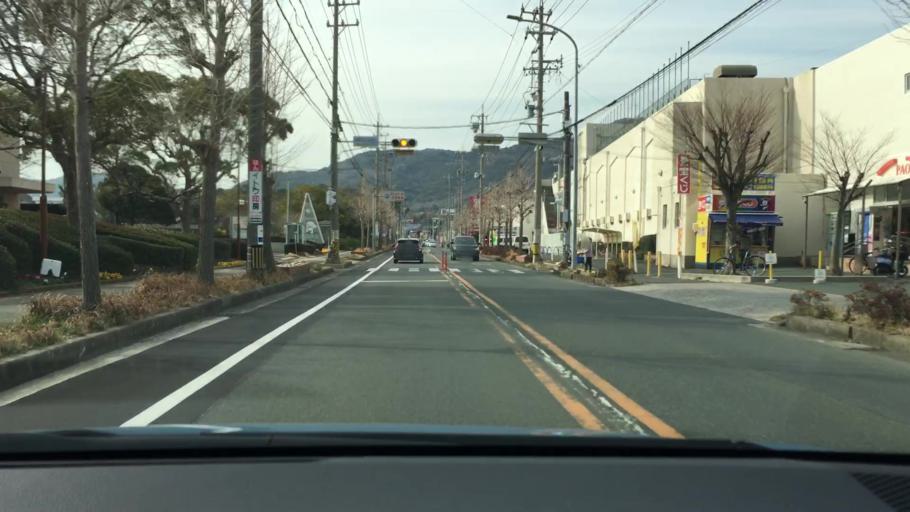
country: JP
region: Aichi
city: Tahara
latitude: 34.6720
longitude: 137.2748
